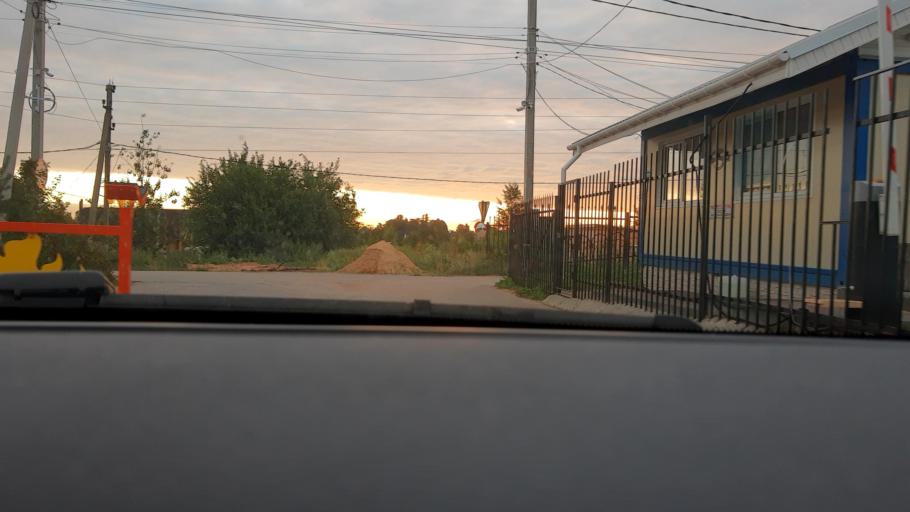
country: RU
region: Nizjnij Novgorod
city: Burevestnik
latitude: 56.1959
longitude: 43.8662
